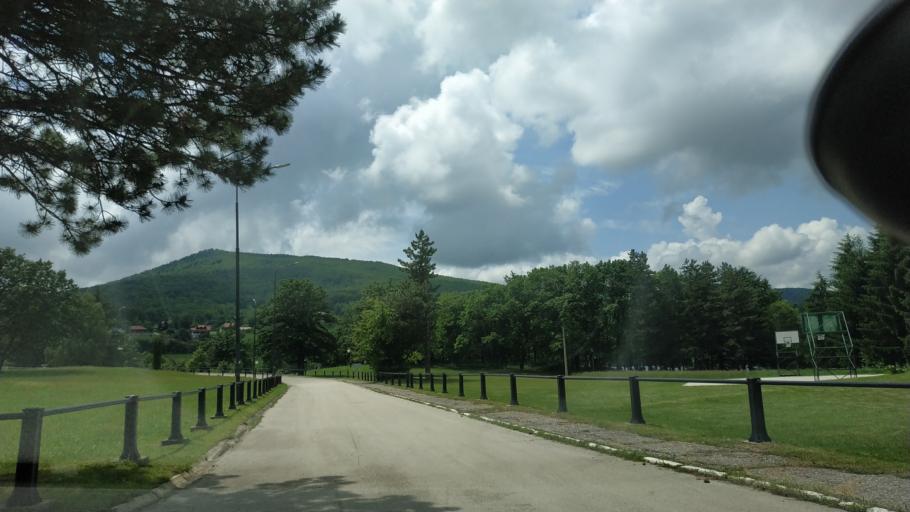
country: RS
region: Central Serbia
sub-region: Borski Okrug
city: Bor
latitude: 44.0902
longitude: 22.0043
